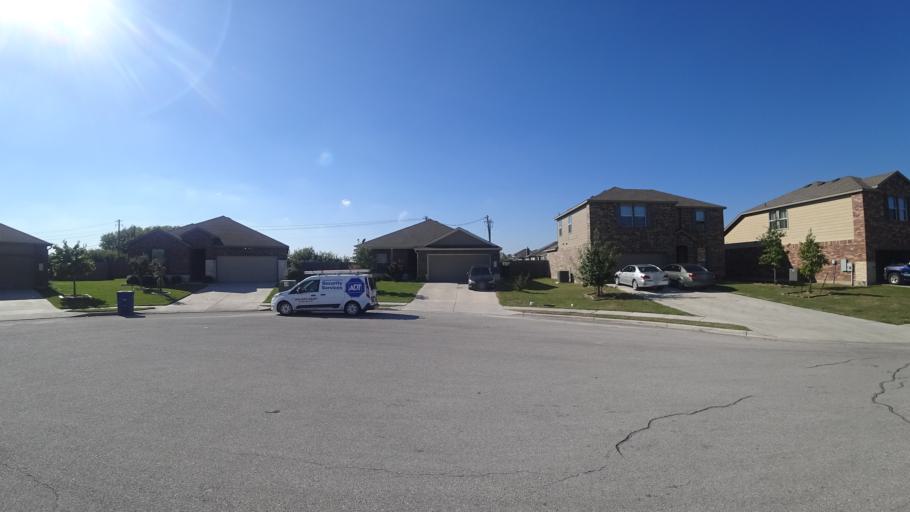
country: US
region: Texas
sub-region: Travis County
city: Manor
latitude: 30.3533
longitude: -97.6184
